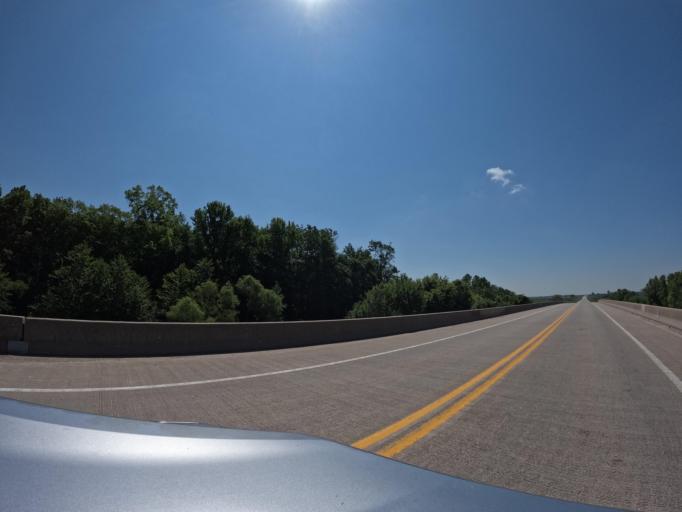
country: US
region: Iowa
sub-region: Keokuk County
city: Sigourney
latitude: 41.3015
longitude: -92.2048
